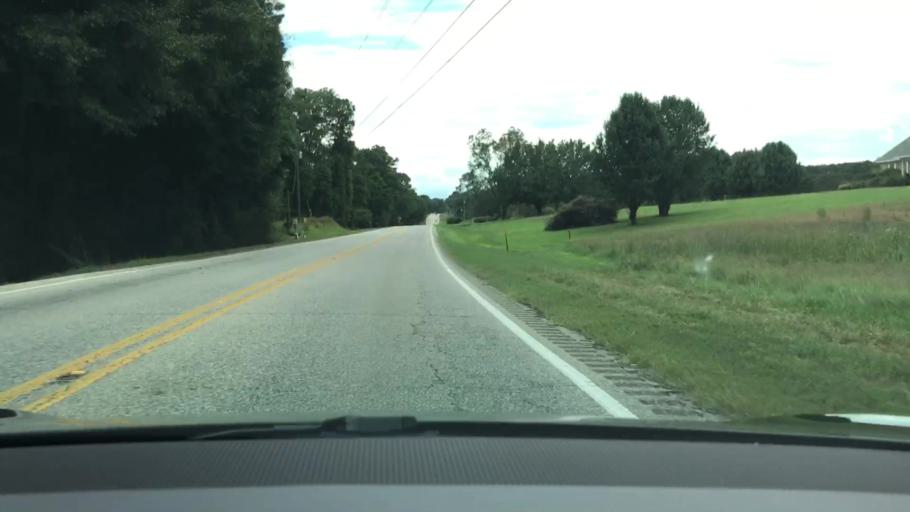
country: US
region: Alabama
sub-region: Pike County
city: Troy
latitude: 31.7385
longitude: -85.9571
